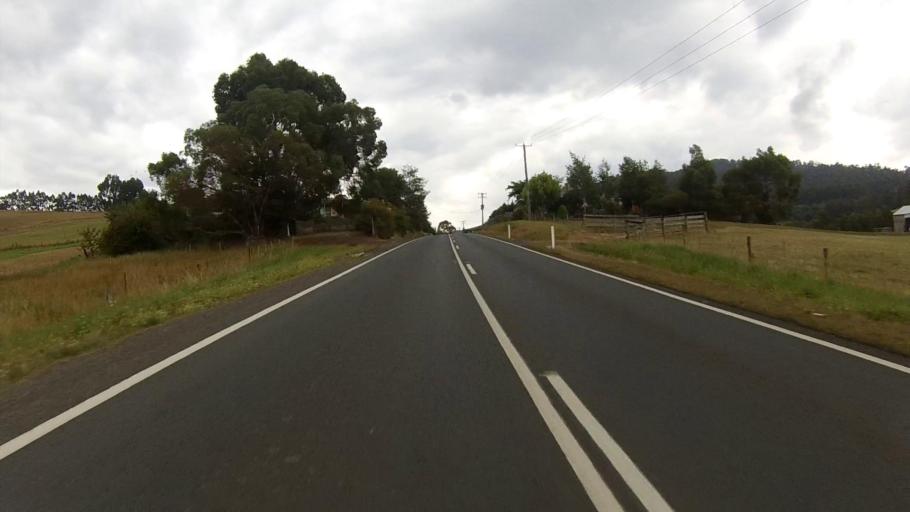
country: AU
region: Tasmania
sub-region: Huon Valley
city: Cygnet
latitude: -43.1469
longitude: 147.0663
